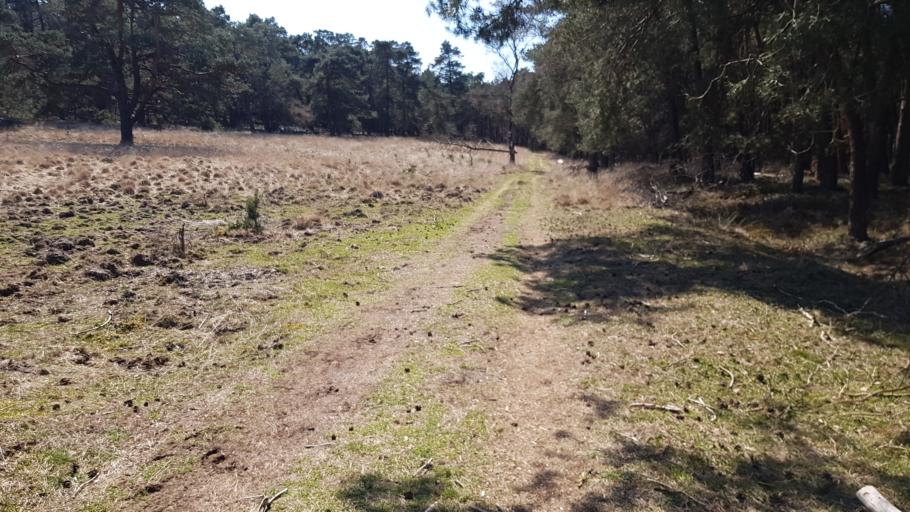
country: NL
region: Gelderland
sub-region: Gemeente Rozendaal
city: Rozendaal
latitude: 52.0588
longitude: 5.9914
